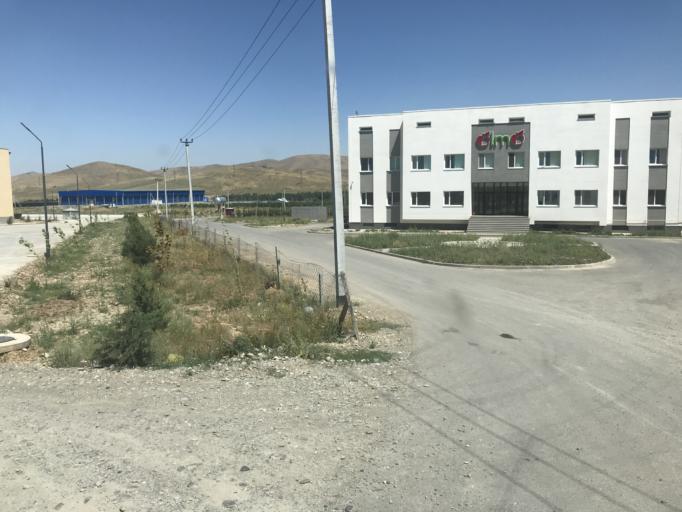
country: KZ
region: Ongtustik Qazaqstan
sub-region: Tulkibas Audany
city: Zhabagly
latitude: 42.5089
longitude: 70.5019
